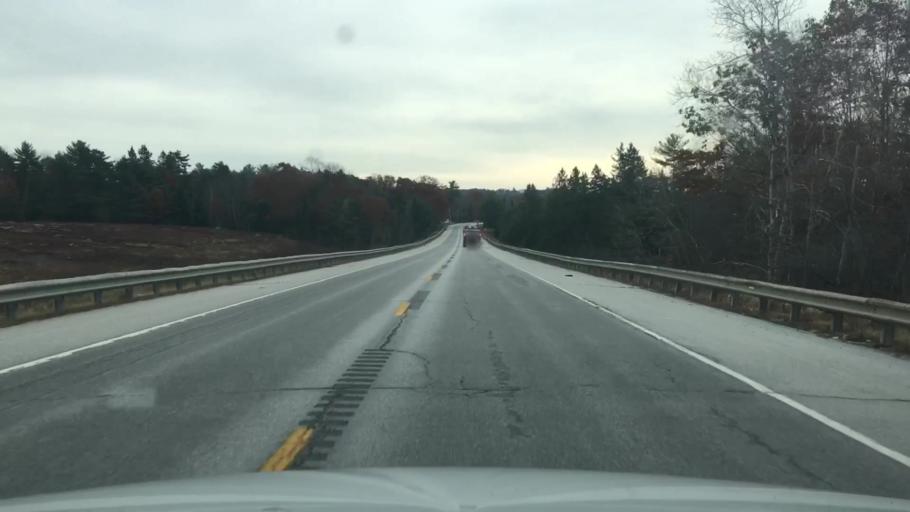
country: US
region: Maine
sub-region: Hancock County
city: Orland
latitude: 44.5694
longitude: -68.7236
